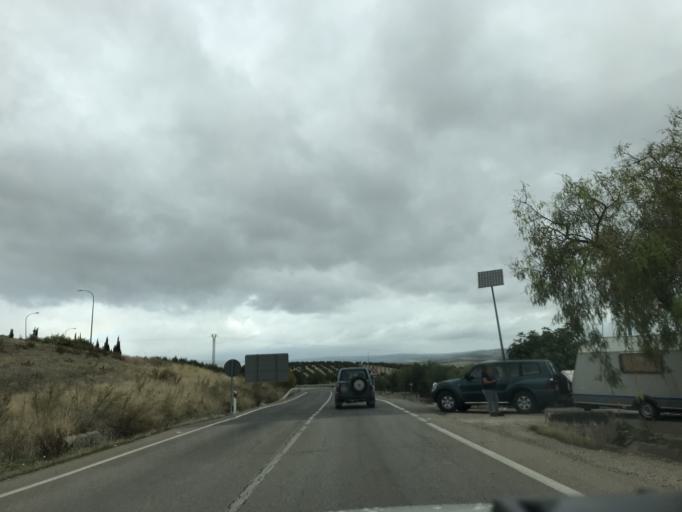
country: ES
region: Andalusia
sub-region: Provincia de Jaen
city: Peal de Becerro
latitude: 37.9195
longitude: -3.1320
